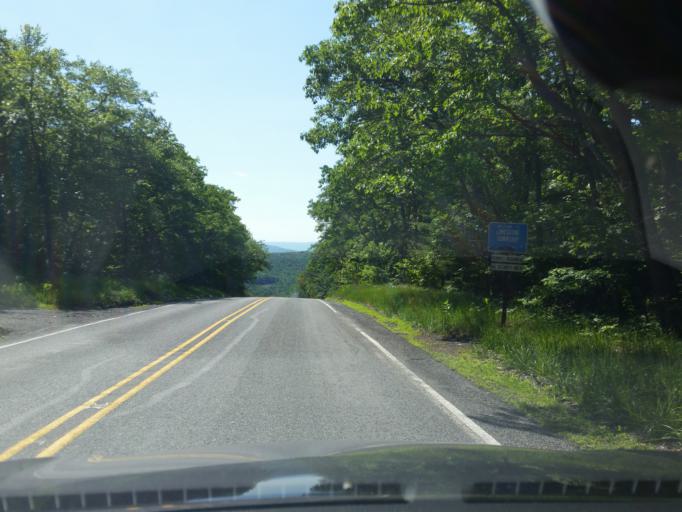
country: US
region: Pennsylvania
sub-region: Lycoming County
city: Duboistown
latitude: 41.1385
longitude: -77.0861
